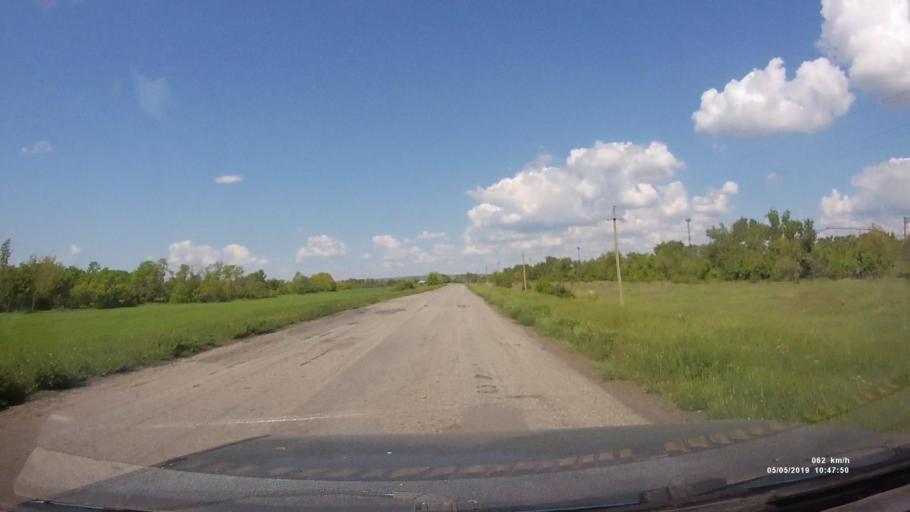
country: RU
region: Rostov
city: Ust'-Donetskiy
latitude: 47.6400
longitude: 40.8278
